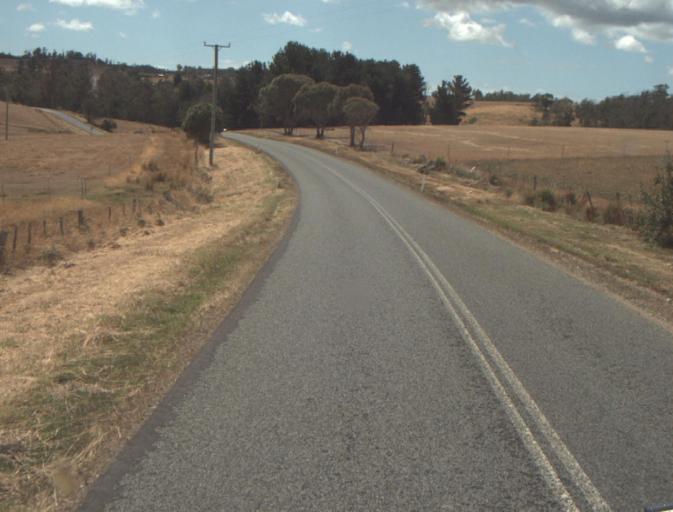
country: AU
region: Tasmania
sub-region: Launceston
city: Mayfield
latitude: -41.2122
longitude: 147.1211
